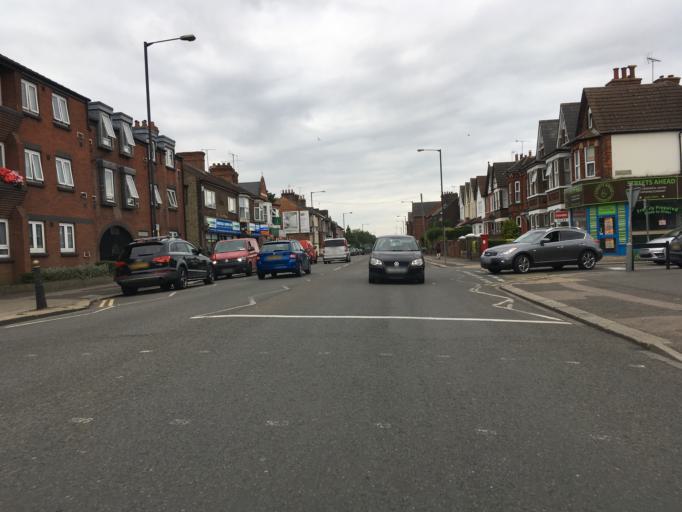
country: GB
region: England
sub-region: Central Bedfordshire
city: Dunstable
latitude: 51.8904
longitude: -0.5269
